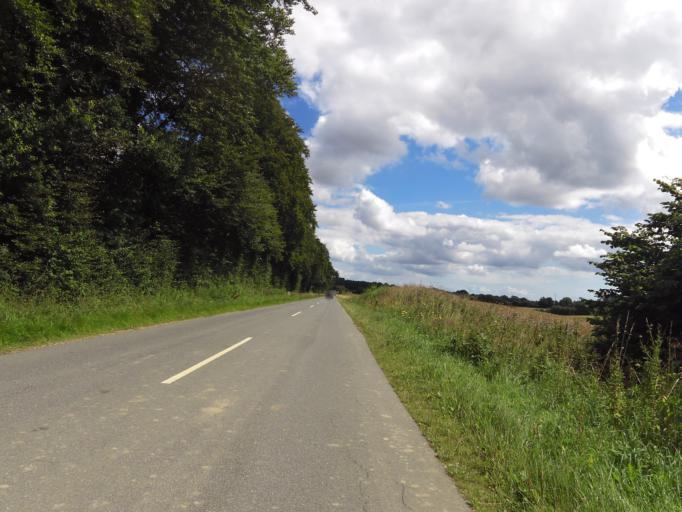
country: DK
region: South Denmark
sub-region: Haderslev Kommune
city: Vojens
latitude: 55.2840
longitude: 9.3870
